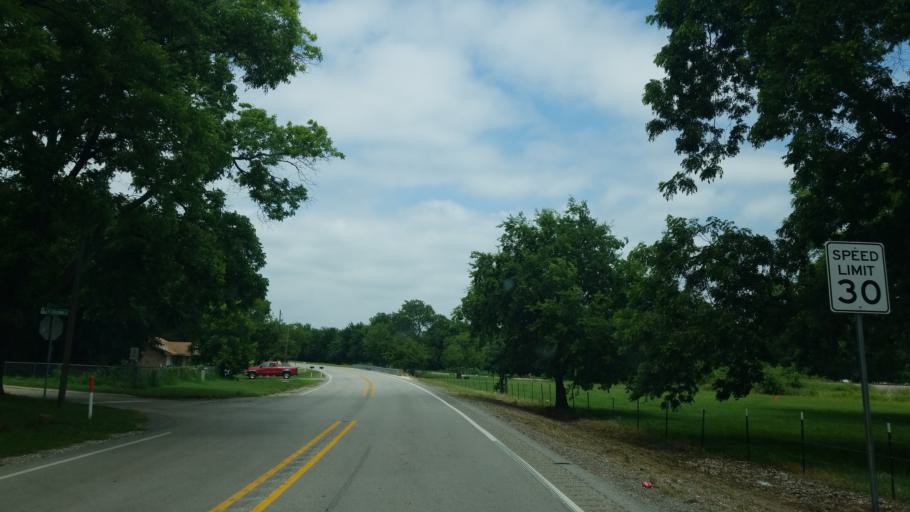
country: US
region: Texas
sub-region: Denton County
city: Aubrey
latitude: 33.3051
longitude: -96.9850
